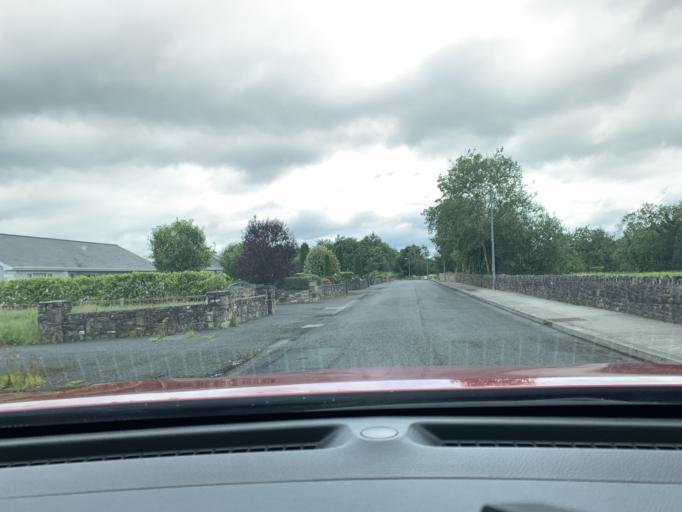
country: IE
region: Connaught
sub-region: Roscommon
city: Boyle
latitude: 53.9827
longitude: -8.2868
